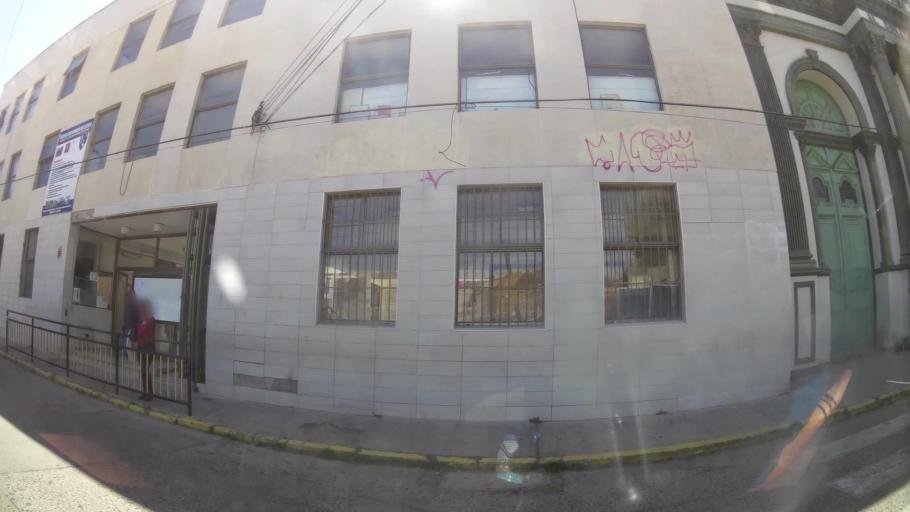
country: CL
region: Valparaiso
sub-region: Provincia de Valparaiso
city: Valparaiso
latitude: -33.0466
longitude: -71.6030
